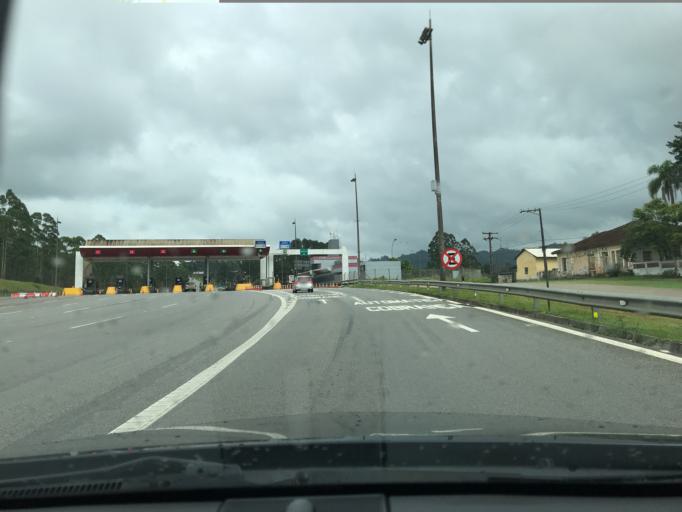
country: BR
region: Sao Paulo
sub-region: Vargem Grande Paulista
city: Vargem Grande Paulista
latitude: -23.5998
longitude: -47.0376
